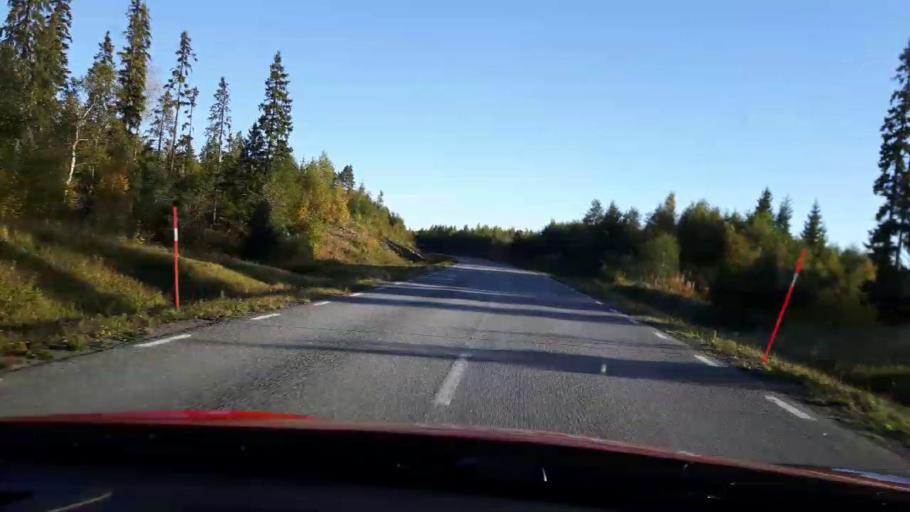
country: SE
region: Jaemtland
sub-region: OEstersunds Kommun
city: Lit
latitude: 63.7806
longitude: 14.7067
